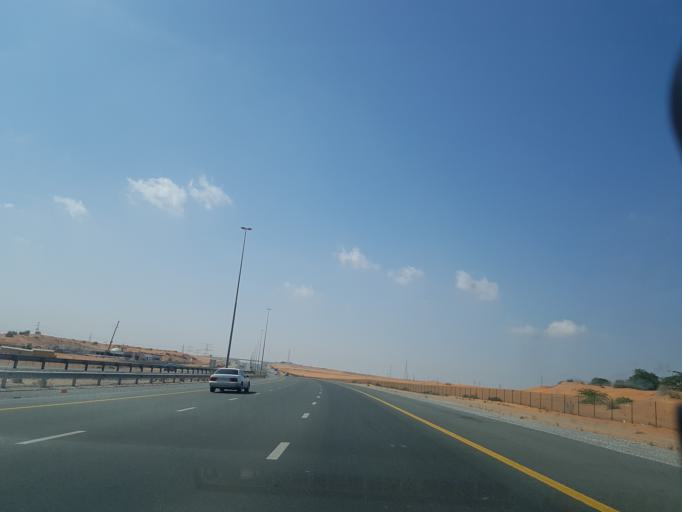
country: AE
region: Ra's al Khaymah
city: Ras al-Khaimah
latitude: 25.7048
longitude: 55.9378
